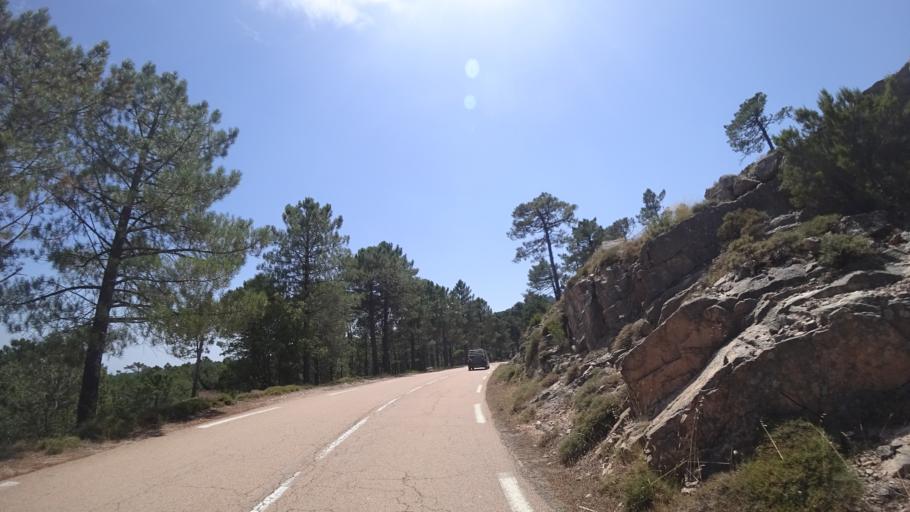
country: FR
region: Corsica
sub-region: Departement de la Corse-du-Sud
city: Zonza
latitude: 41.6836
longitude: 9.2016
